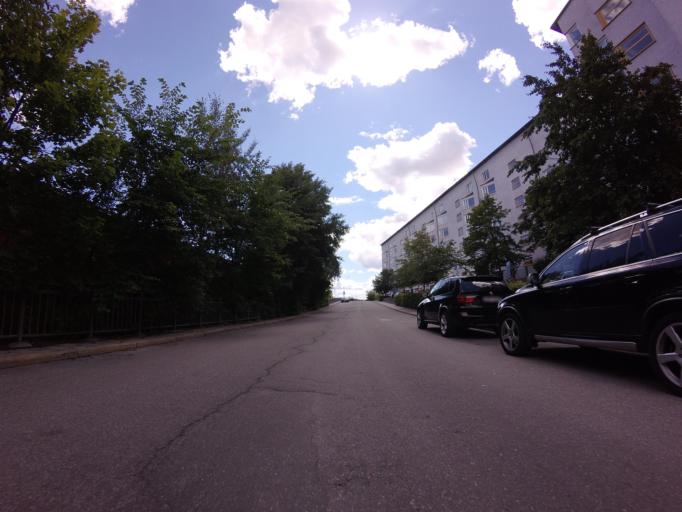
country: SE
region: Stockholm
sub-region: Stockholms Kommun
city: Stockholm
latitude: 59.3515
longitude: 18.0639
